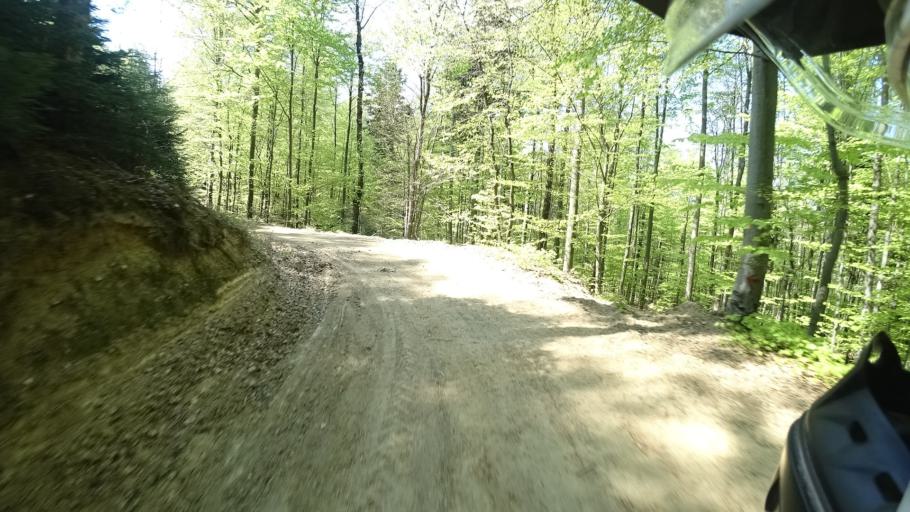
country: HR
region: Zagrebacka
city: Jablanovec
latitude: 45.9040
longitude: 15.9178
